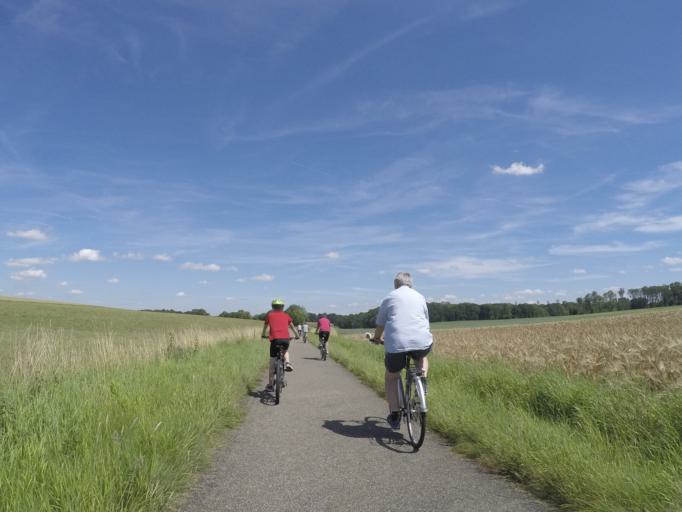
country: BE
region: Wallonia
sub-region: Province de Namur
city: Havelange
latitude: 50.3747
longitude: 5.2312
